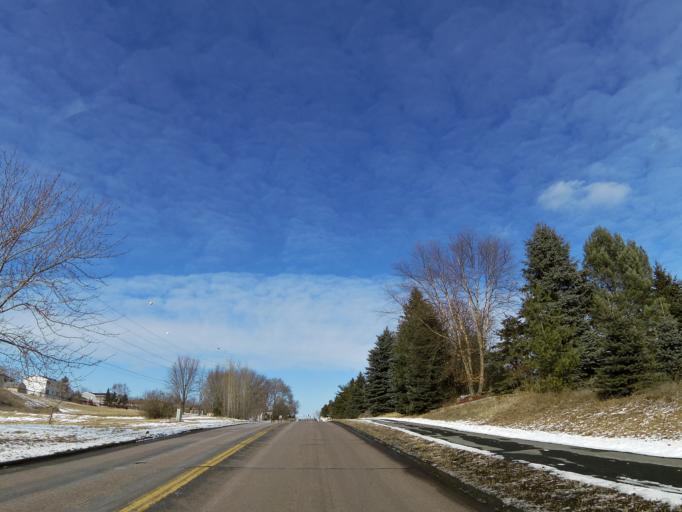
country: US
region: Minnesota
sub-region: Hennepin County
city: Eden Prairie
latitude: 44.8253
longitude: -93.4291
